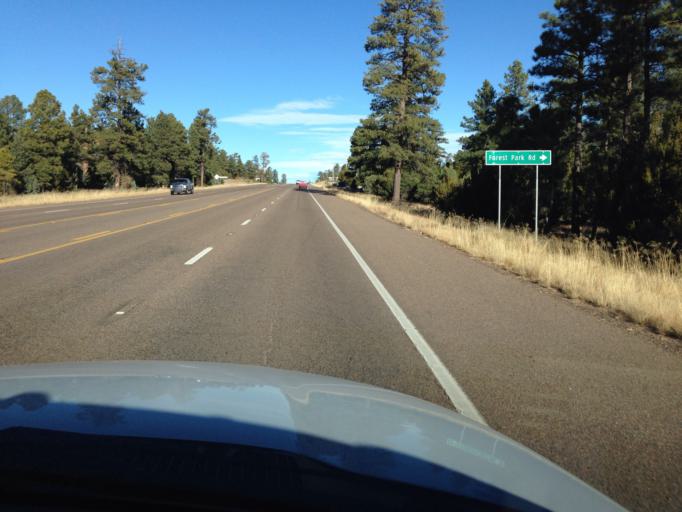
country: US
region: Arizona
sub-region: Navajo County
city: Heber-Overgaard
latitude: 34.4068
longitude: -110.5668
